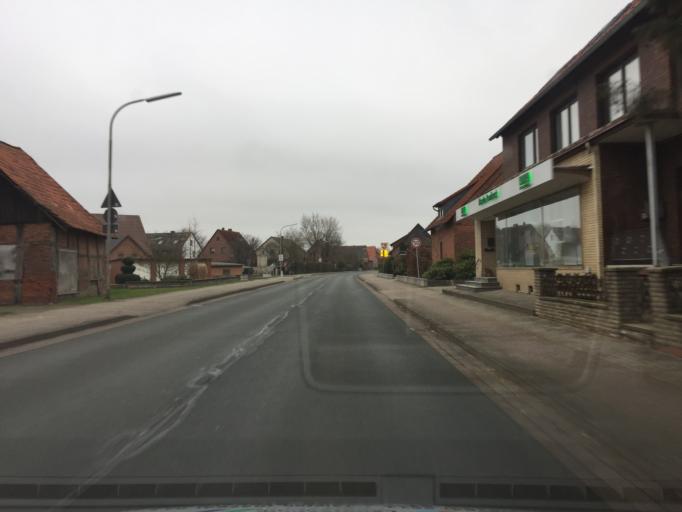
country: DE
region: Lower Saxony
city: Niedernwohren
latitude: 52.3546
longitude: 9.1429
